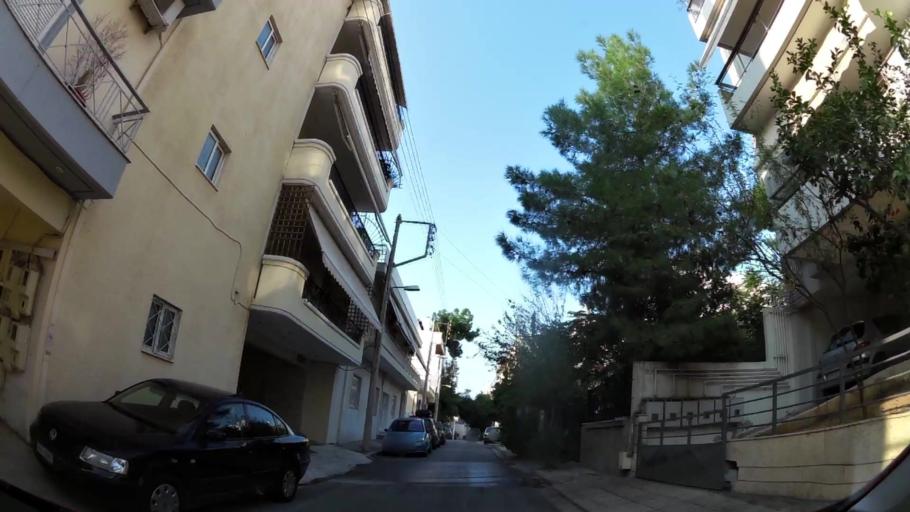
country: GR
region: Attica
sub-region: Nomarchia Athinas
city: Dhafni
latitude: 37.9506
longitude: 23.7270
